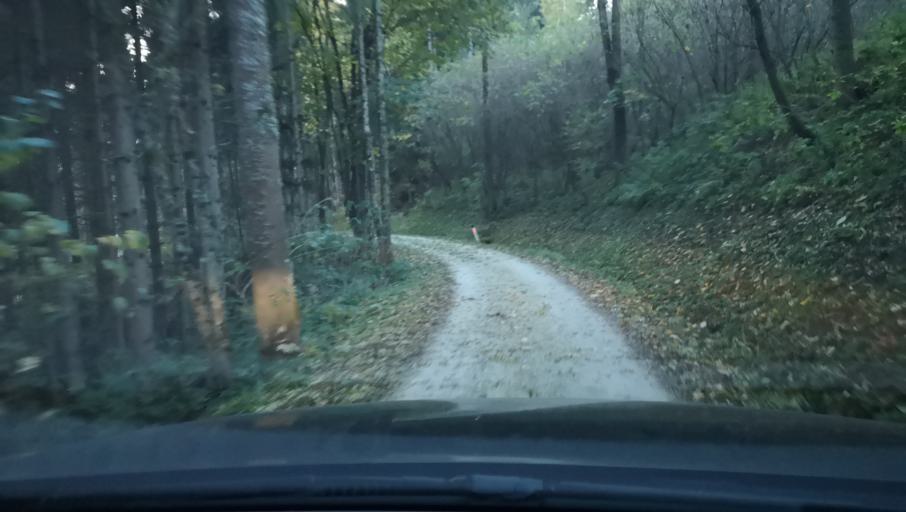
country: AT
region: Styria
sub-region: Politischer Bezirk Weiz
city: Birkfeld
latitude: 47.3634
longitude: 15.6607
